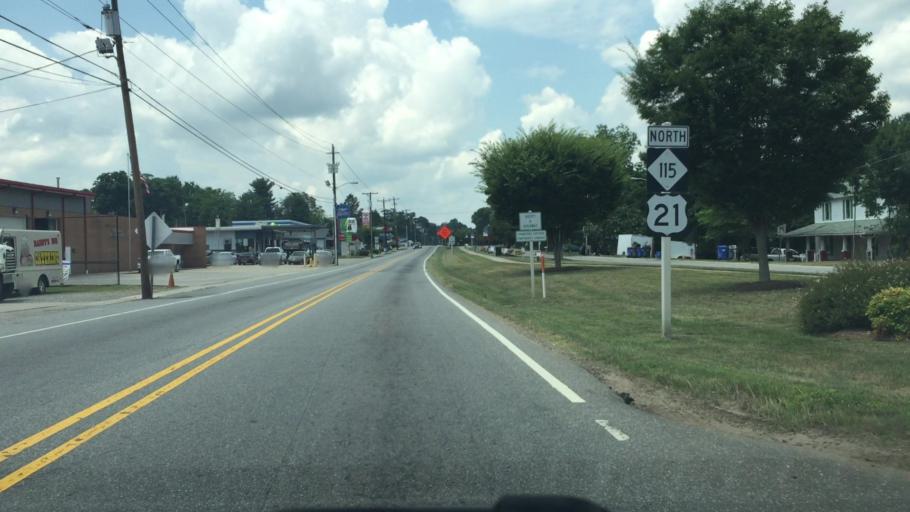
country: US
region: North Carolina
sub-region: Iredell County
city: Troutman
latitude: 35.7022
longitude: -80.8891
